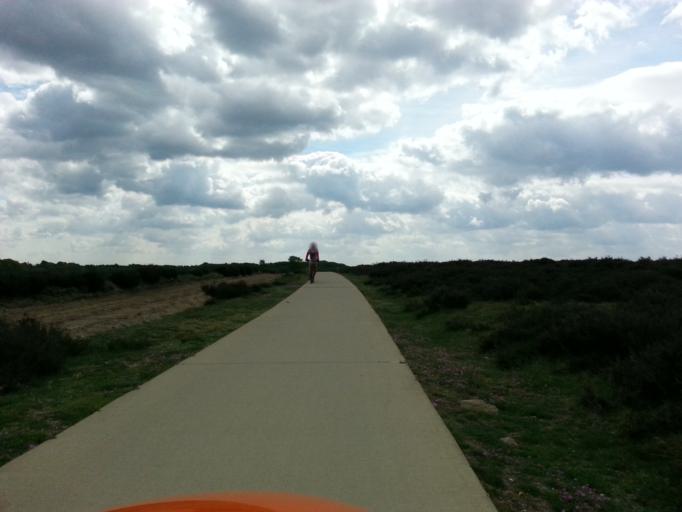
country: NL
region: Gelderland
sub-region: Gemeente Ede
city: Ede
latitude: 52.0435
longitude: 5.7157
